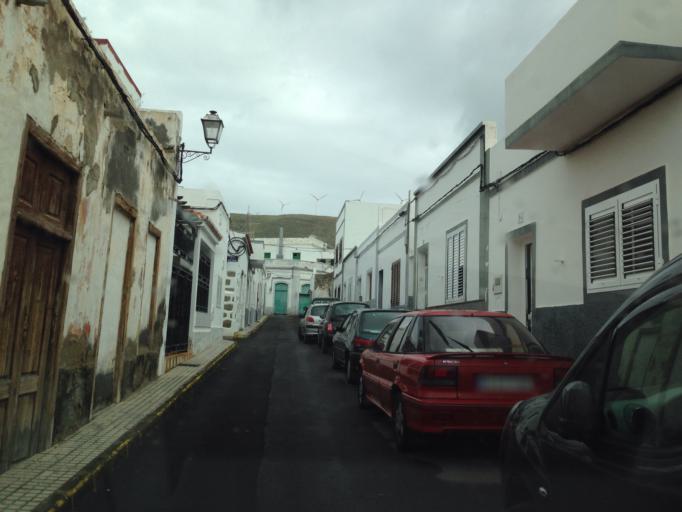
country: ES
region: Canary Islands
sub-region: Provincia de Las Palmas
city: Agaete
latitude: 28.0981
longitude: -15.6974
